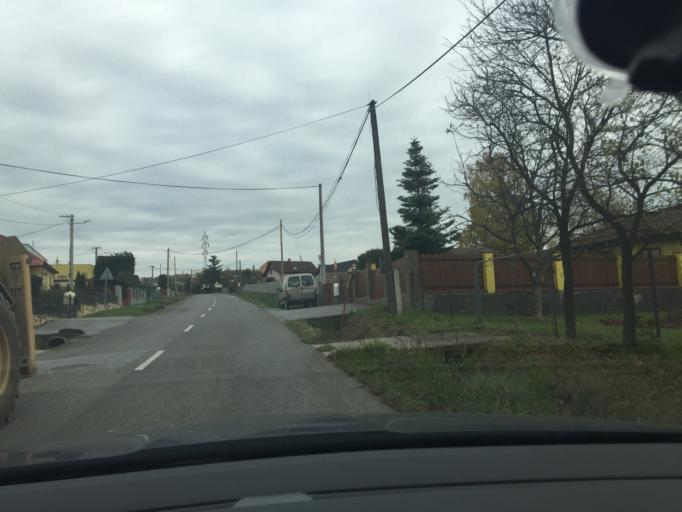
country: SK
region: Presovsky
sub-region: Okres Presov
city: Presov
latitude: 48.9472
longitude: 21.2883
